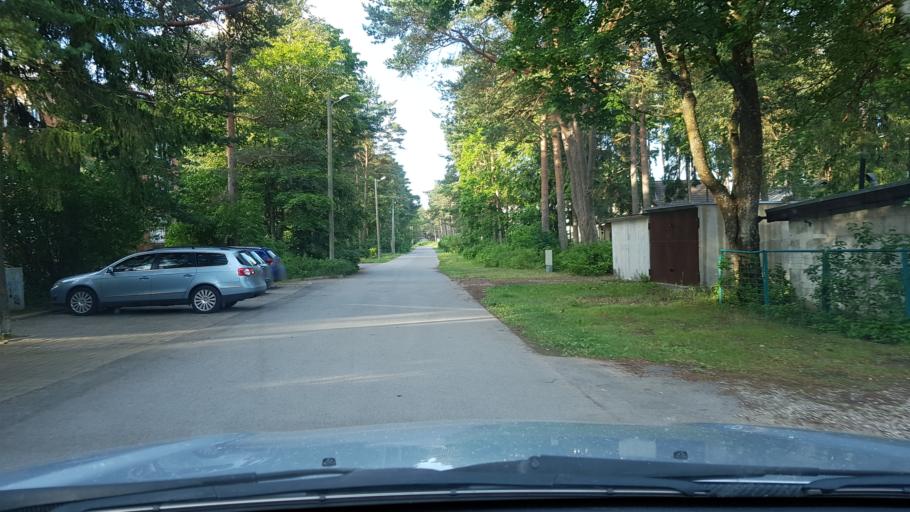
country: EE
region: Ida-Virumaa
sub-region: Narva-Joesuu linn
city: Narva-Joesuu
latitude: 59.4578
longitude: 28.0477
